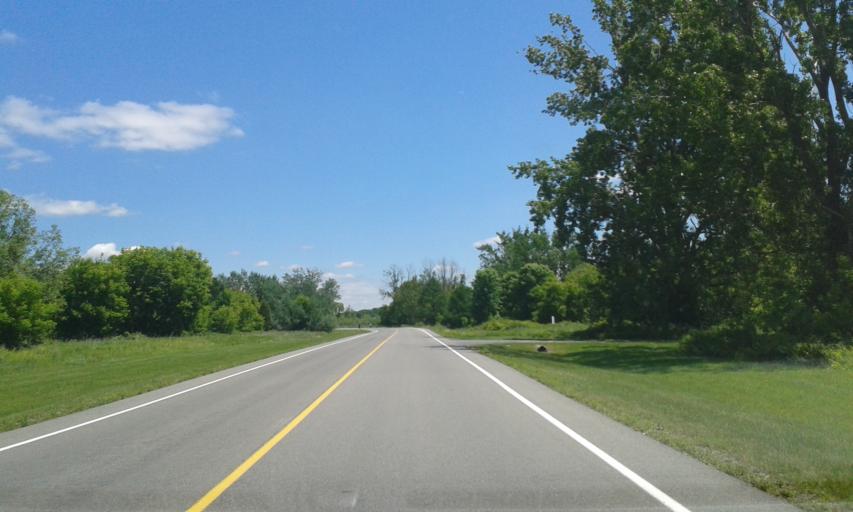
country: US
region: New York
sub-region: St. Lawrence County
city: Massena
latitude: 44.9970
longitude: -74.9065
